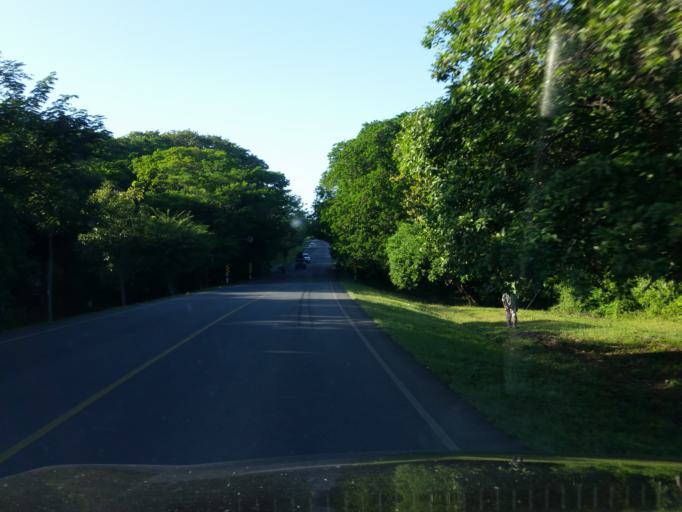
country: NI
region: Rivas
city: Rivas
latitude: 11.4186
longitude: -85.7999
